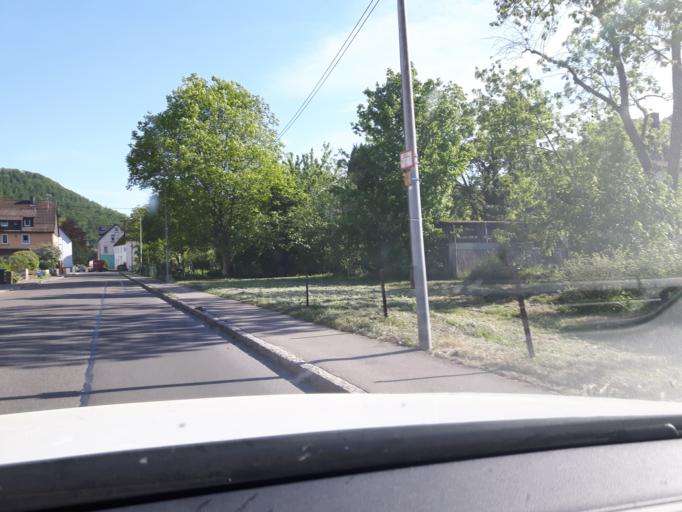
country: DE
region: Baden-Wuerttemberg
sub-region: Tuebingen Region
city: Pfullingen
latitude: 48.4362
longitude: 9.2565
